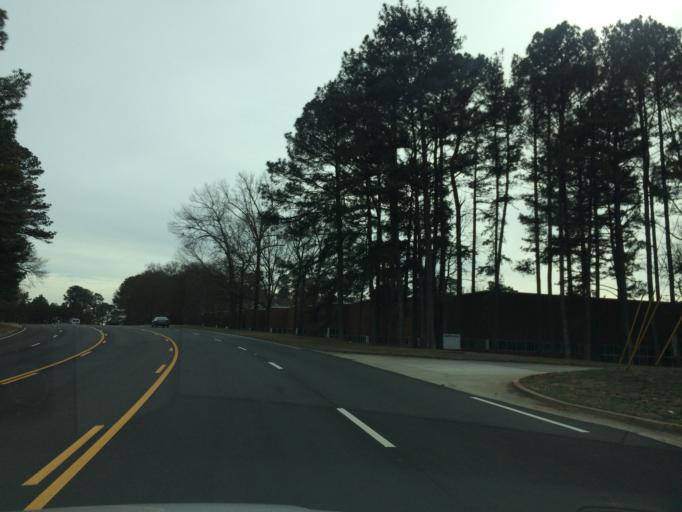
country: US
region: Georgia
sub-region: Gwinnett County
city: Duluth
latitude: 33.9745
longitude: -84.1009
